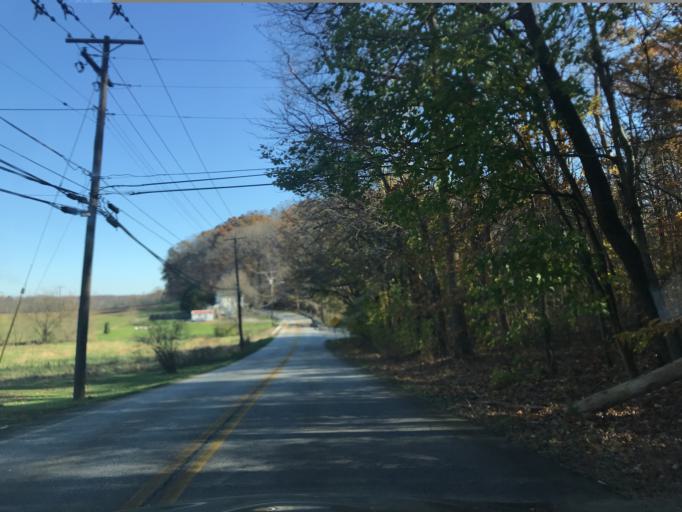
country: US
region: Maryland
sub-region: Baltimore County
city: Perry Hall
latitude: 39.4569
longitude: -76.4823
